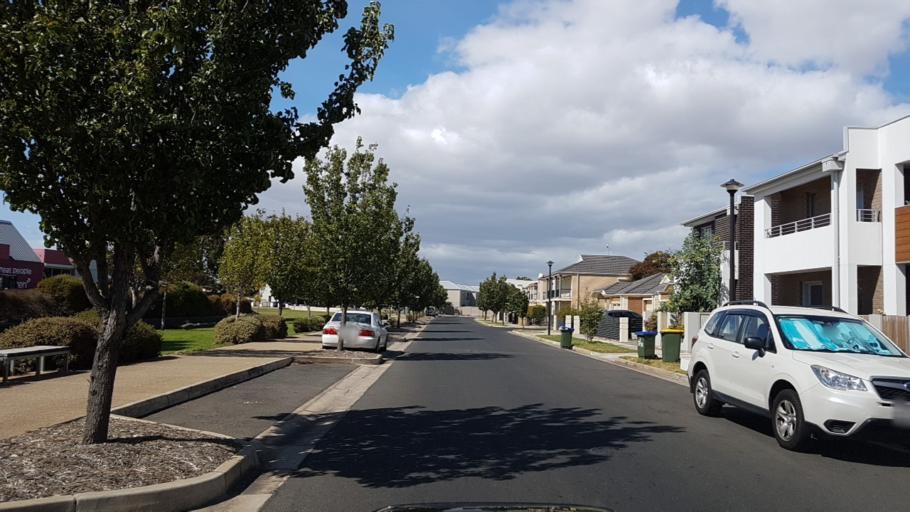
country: AU
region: South Australia
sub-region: Charles Sturt
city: Woodville North
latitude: -34.8572
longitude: 138.5441
